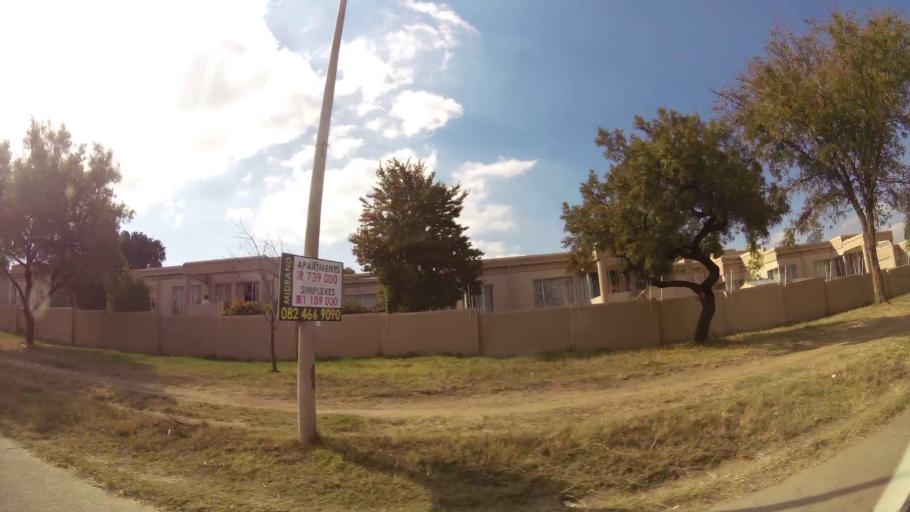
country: ZA
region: Gauteng
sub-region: City of Johannesburg Metropolitan Municipality
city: Midrand
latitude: -25.9911
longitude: 28.1142
